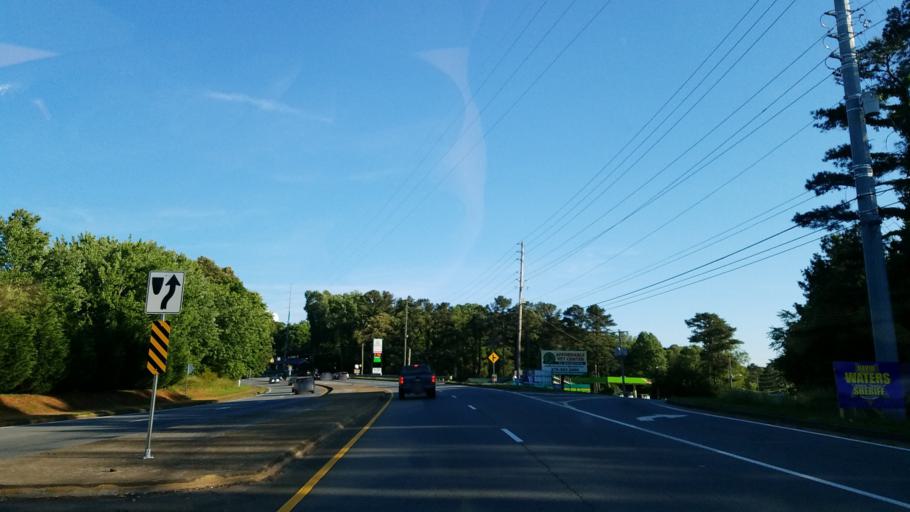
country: US
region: Georgia
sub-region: Cherokee County
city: Woodstock
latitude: 34.1217
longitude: -84.5860
